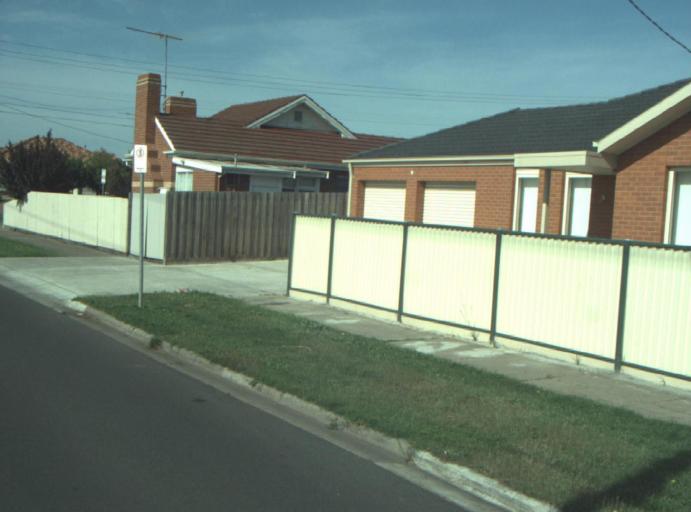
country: AU
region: Victoria
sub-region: Greater Geelong
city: Bell Park
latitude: -38.1095
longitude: 144.3376
